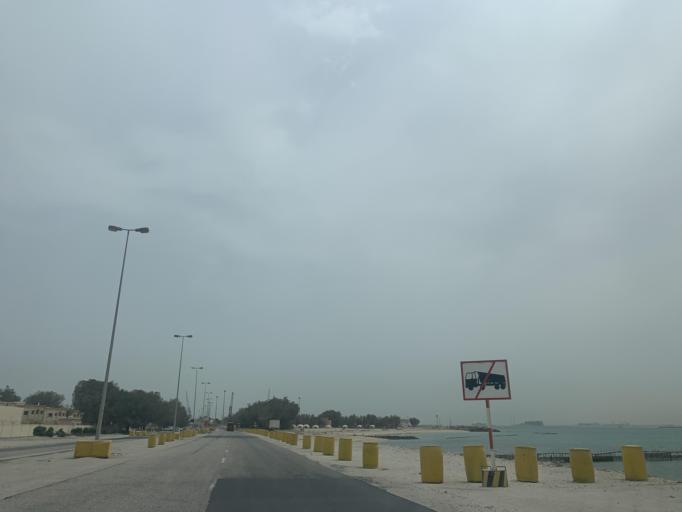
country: BH
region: Muharraq
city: Al Hadd
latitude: 26.1997
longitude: 50.6617
